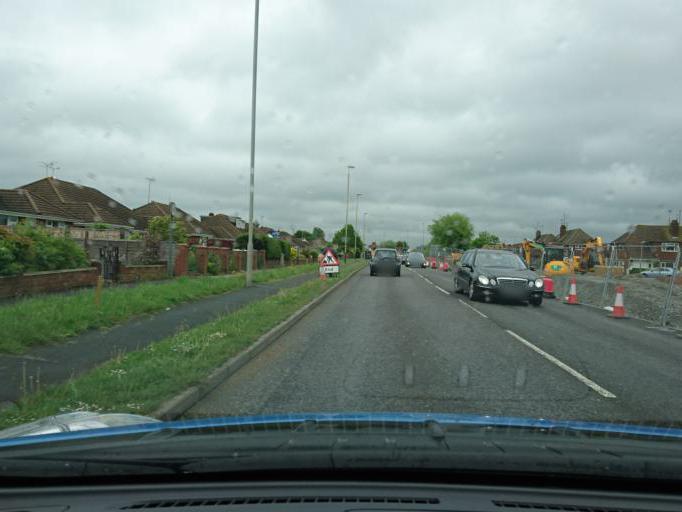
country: GB
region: England
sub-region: Borough of Swindon
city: Swindon
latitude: 51.5720
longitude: -1.7499
